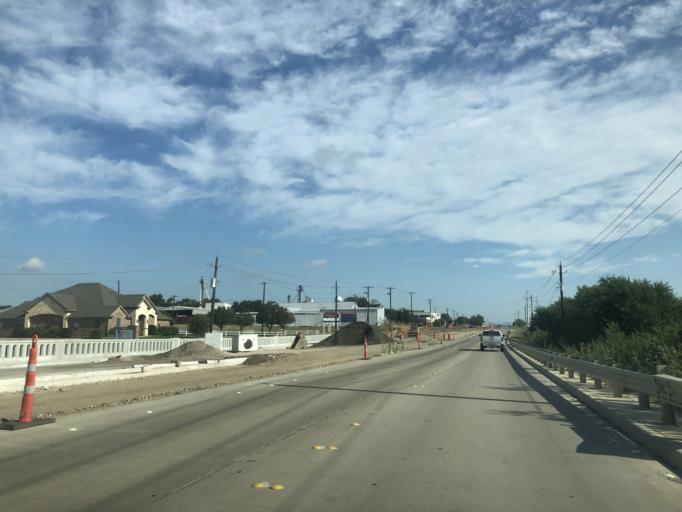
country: US
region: Texas
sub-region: Denton County
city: Justin
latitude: 33.0782
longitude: -97.2958
